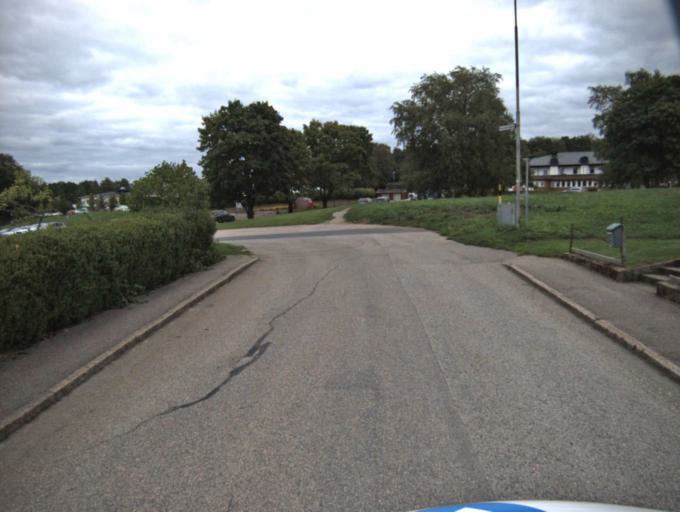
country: SE
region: Vaestra Goetaland
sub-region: Ulricehamns Kommun
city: Ulricehamn
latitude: 57.8009
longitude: 13.4331
